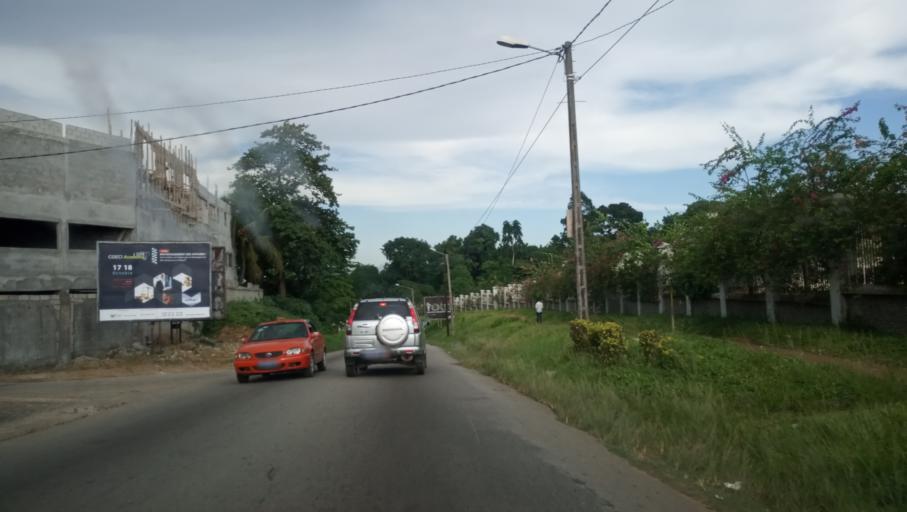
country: CI
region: Lagunes
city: Abidjan
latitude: 5.3497
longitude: -3.9859
